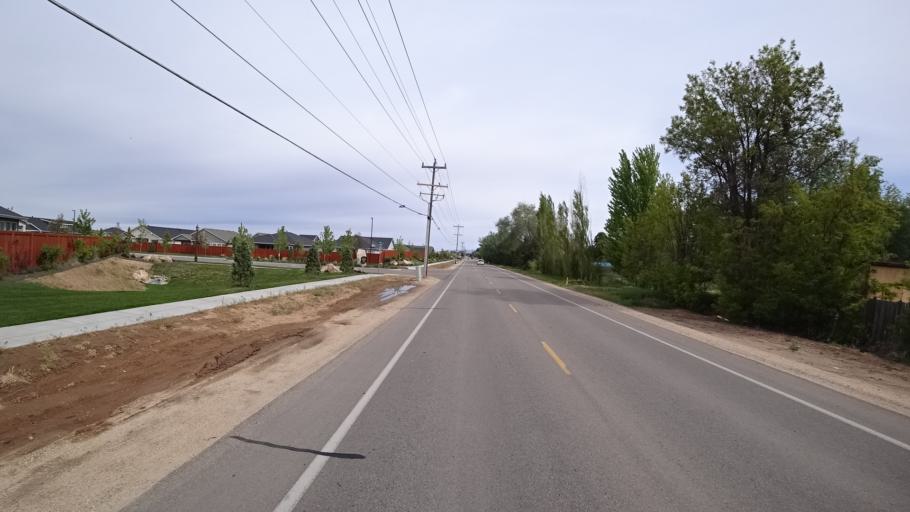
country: US
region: Idaho
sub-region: Ada County
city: Meridian
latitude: 43.5411
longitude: -116.3145
